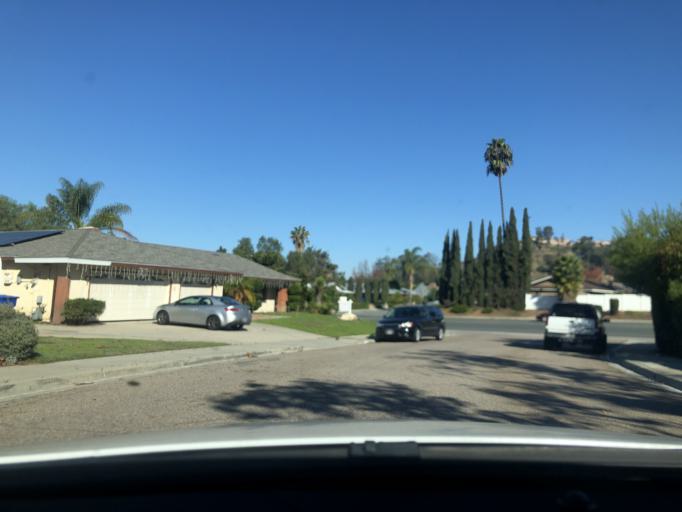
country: US
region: California
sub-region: San Diego County
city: El Cajon
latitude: 32.7794
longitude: -116.9463
